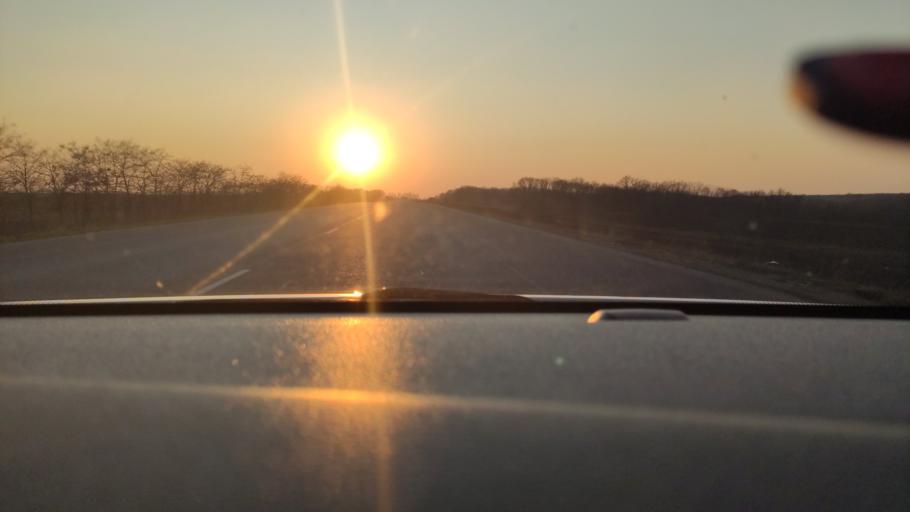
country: RU
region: Voronezj
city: Kolodeznyy
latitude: 51.3395
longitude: 39.0496
